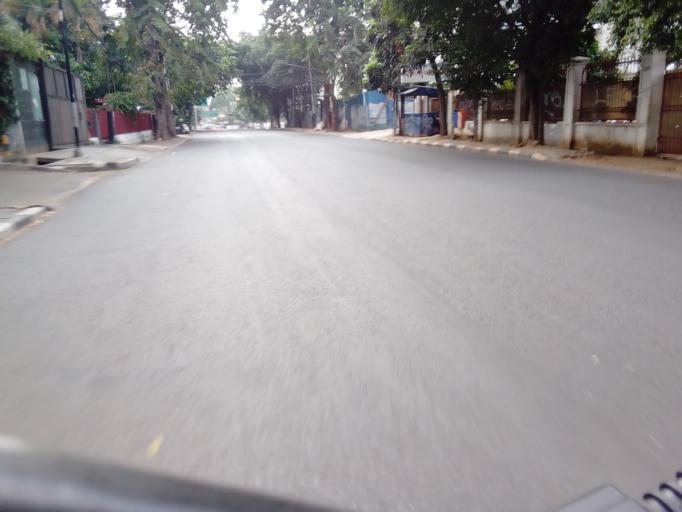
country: ID
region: Jakarta Raya
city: Jakarta
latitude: -6.2035
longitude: 106.8079
